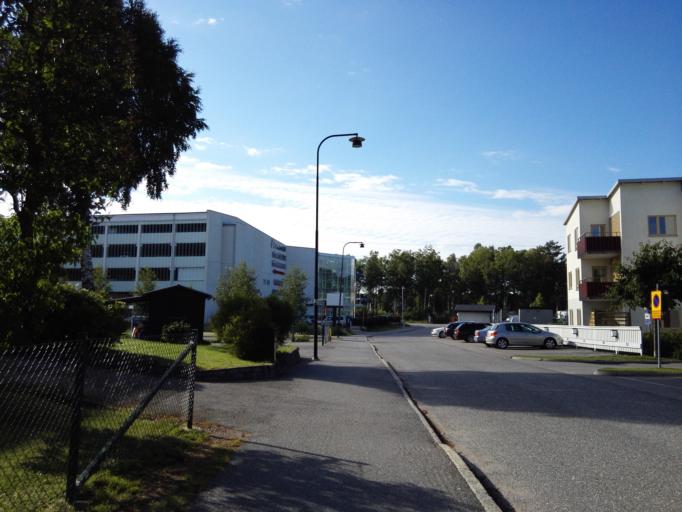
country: SE
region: Stockholm
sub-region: Huddinge Kommun
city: Segeltorp
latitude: 59.2822
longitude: 17.9346
